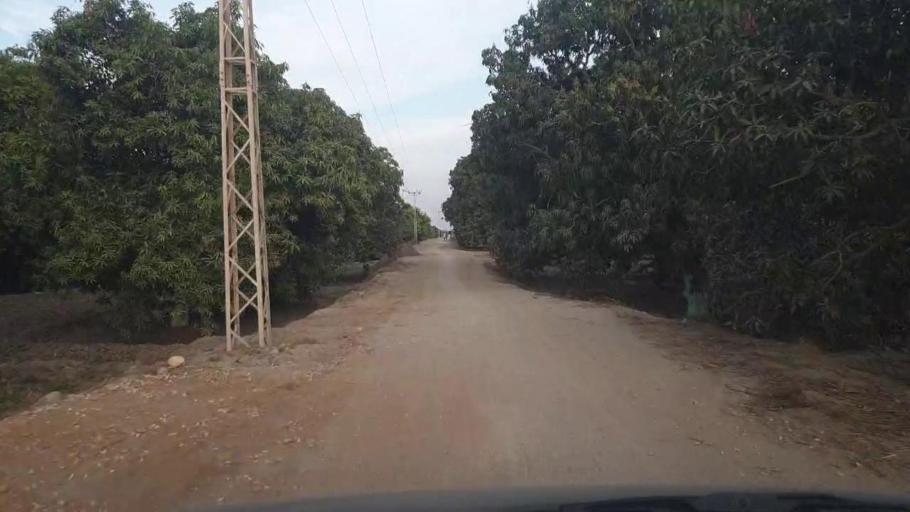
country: PK
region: Sindh
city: Kunri
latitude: 25.2385
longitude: 69.5640
